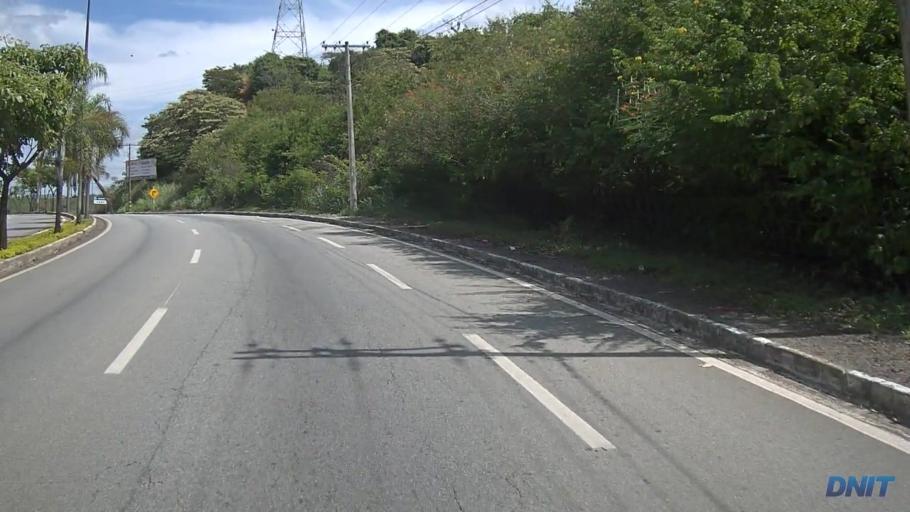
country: BR
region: Minas Gerais
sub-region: Coronel Fabriciano
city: Coronel Fabriciano
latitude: -19.5046
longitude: -42.5916
